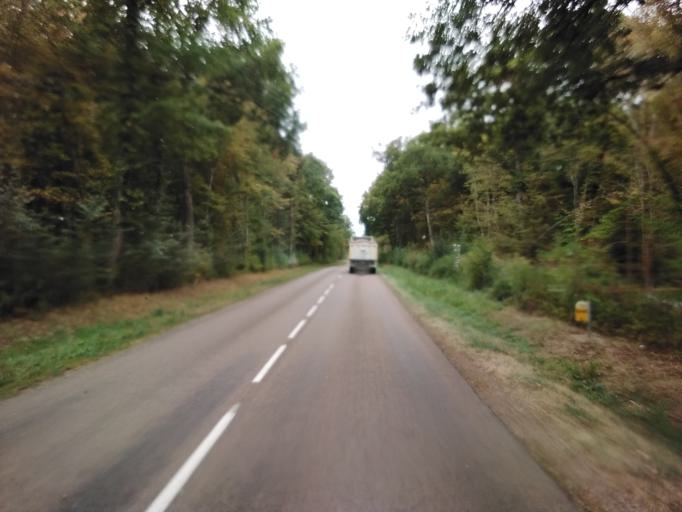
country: FR
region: Champagne-Ardenne
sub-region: Departement de l'Aube
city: Vendeuvre-sur-Barse
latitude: 48.2519
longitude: 4.4890
